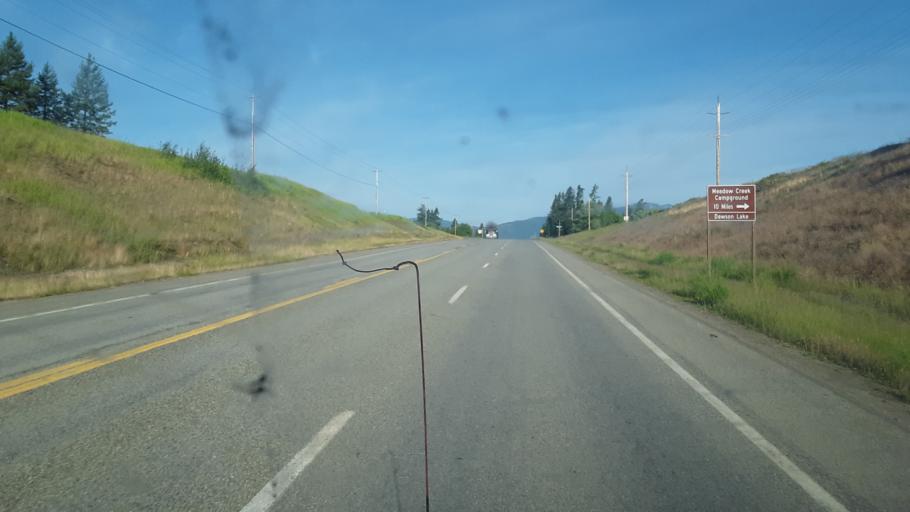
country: US
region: Idaho
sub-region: Boundary County
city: Bonners Ferry
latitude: 48.7317
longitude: -116.2542
